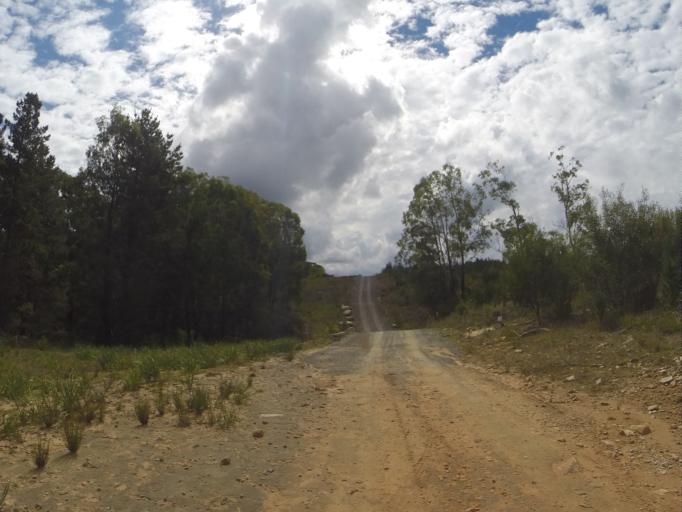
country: AU
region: New South Wales
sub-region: Wingecarribee
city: Moss Vale
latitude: -34.5247
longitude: 150.2247
